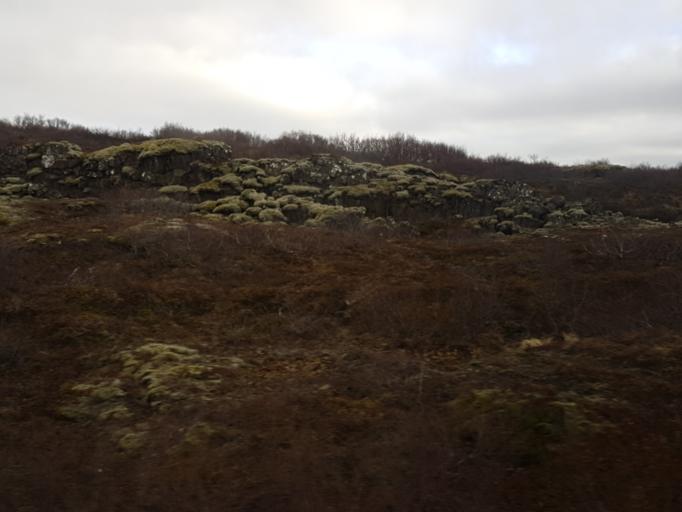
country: IS
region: South
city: Hveragerdi
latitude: 64.2323
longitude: -21.0493
